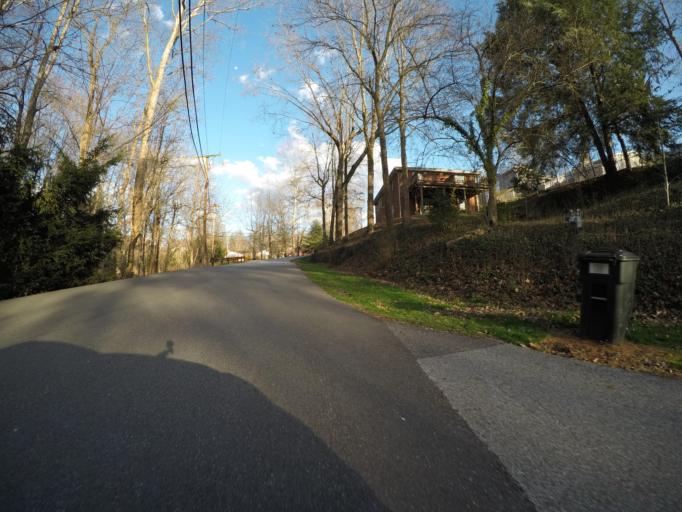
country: US
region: West Virginia
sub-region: Kanawha County
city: Charleston
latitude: 38.3894
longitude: -81.5922
